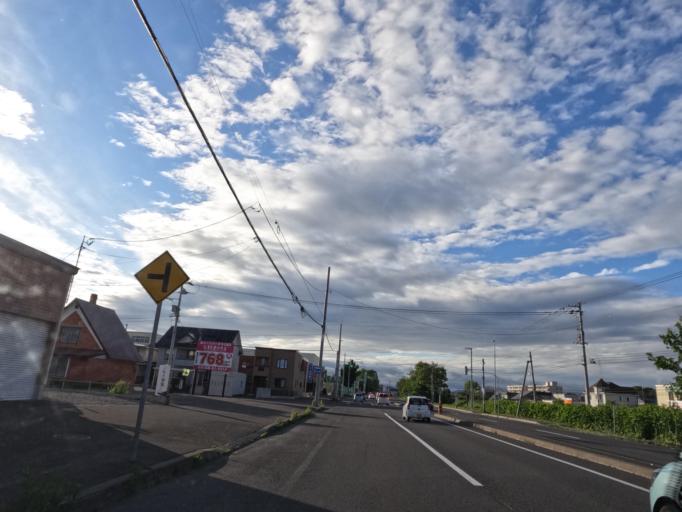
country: JP
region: Hokkaido
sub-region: Asahikawa-shi
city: Asahikawa
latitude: 43.7416
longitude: 142.3591
